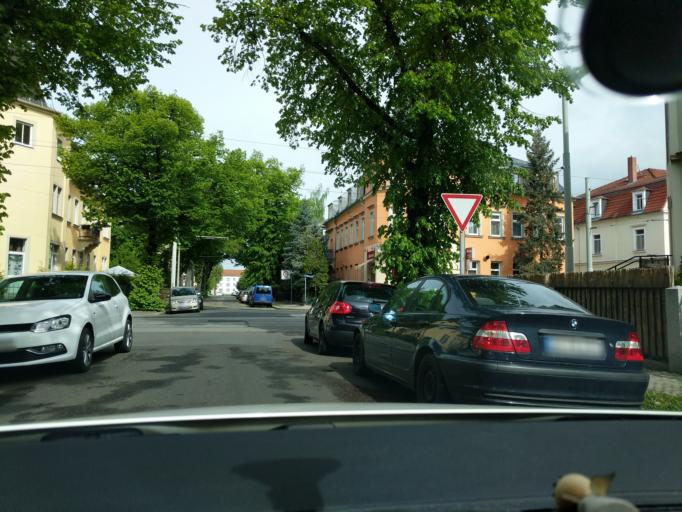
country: DE
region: Saxony
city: Heidenau
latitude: 51.0070
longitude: 13.8288
